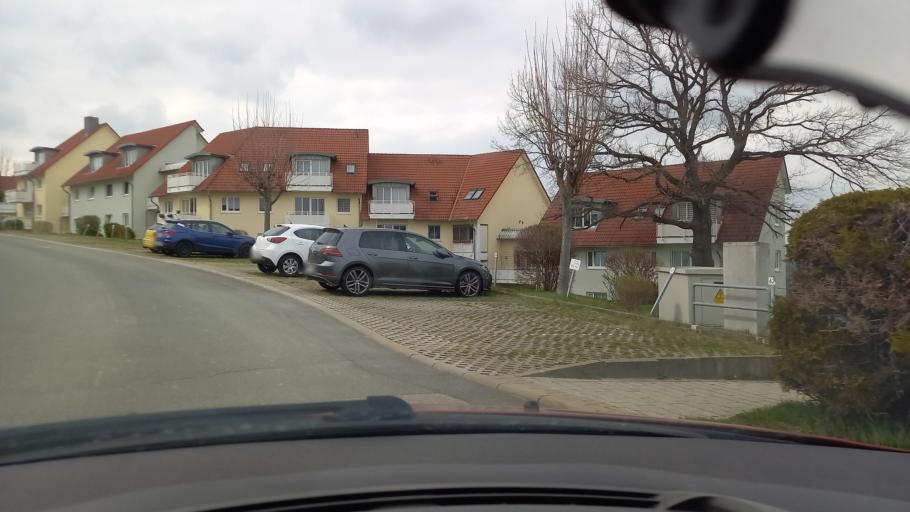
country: DE
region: Saxony
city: Wilkau-Hasslau
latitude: 50.6787
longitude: 12.4963
